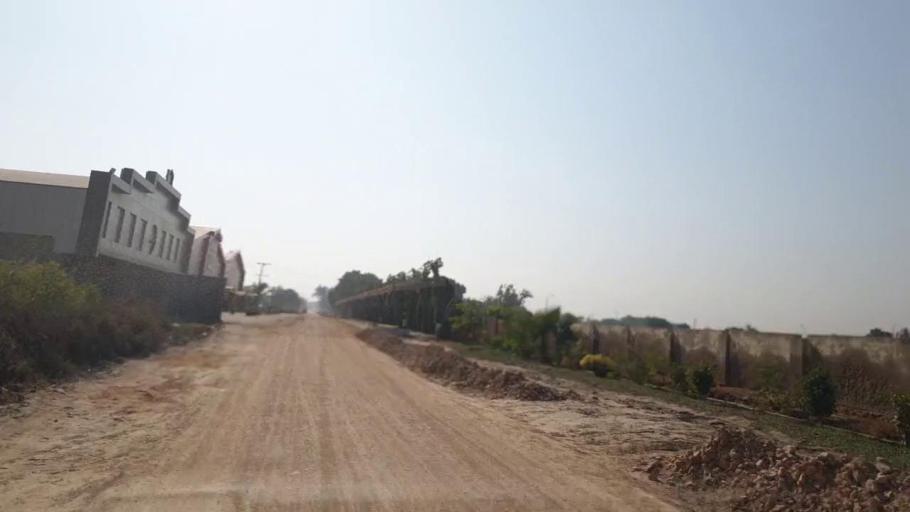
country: PK
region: Sindh
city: Thatta
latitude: 24.7590
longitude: 67.9167
